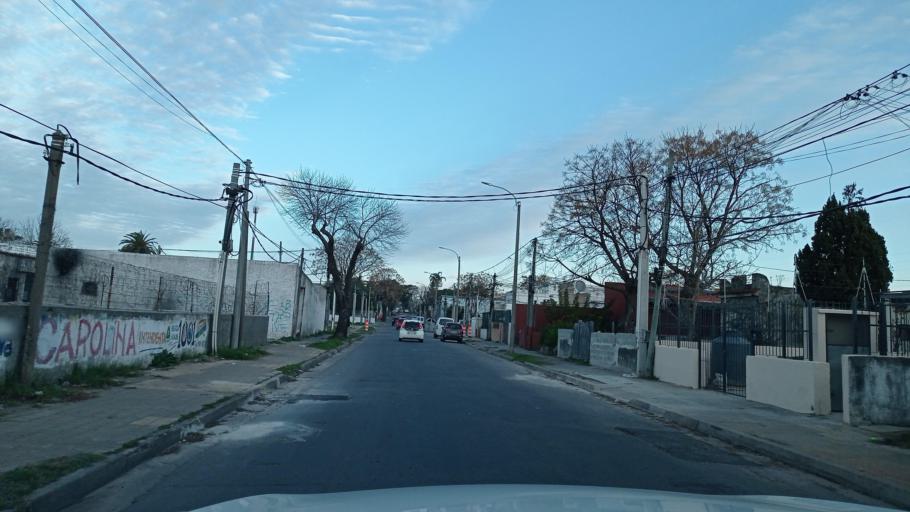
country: UY
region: Montevideo
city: Montevideo
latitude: -34.8685
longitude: -56.1461
